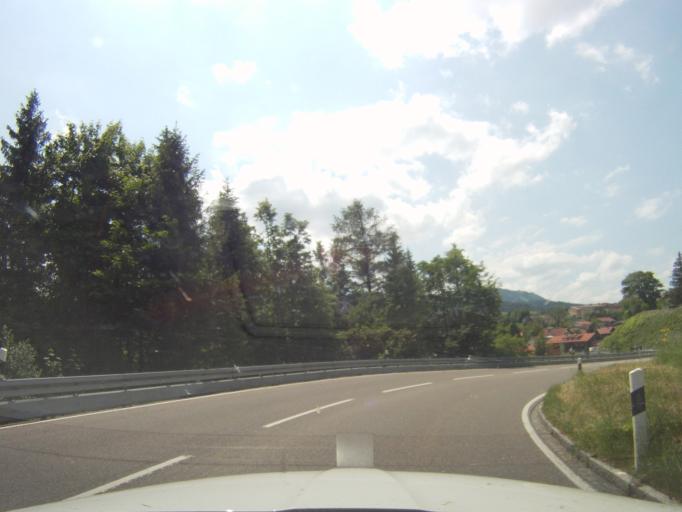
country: DE
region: Bavaria
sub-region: Swabia
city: Nesselwang
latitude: 47.6244
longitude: 10.4994
